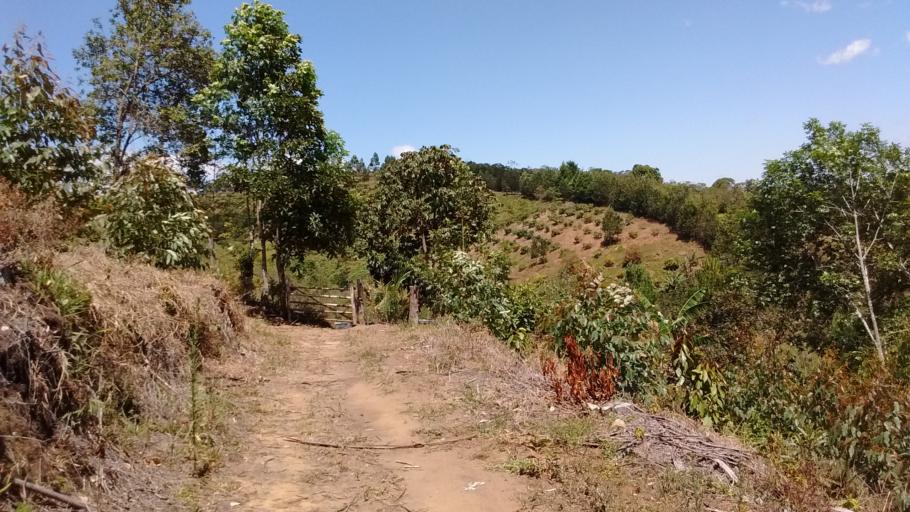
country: CO
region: Cauca
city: Popayan
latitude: 2.4581
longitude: -76.5662
